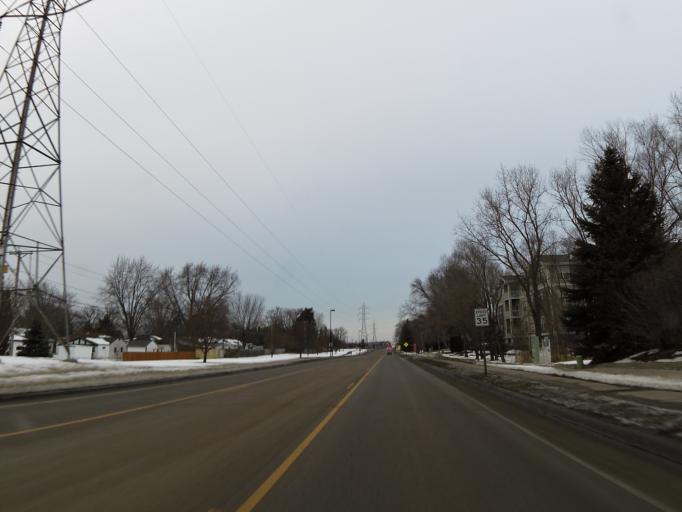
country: US
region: Minnesota
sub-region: Washington County
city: Oakdale
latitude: 44.9663
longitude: -92.9645
